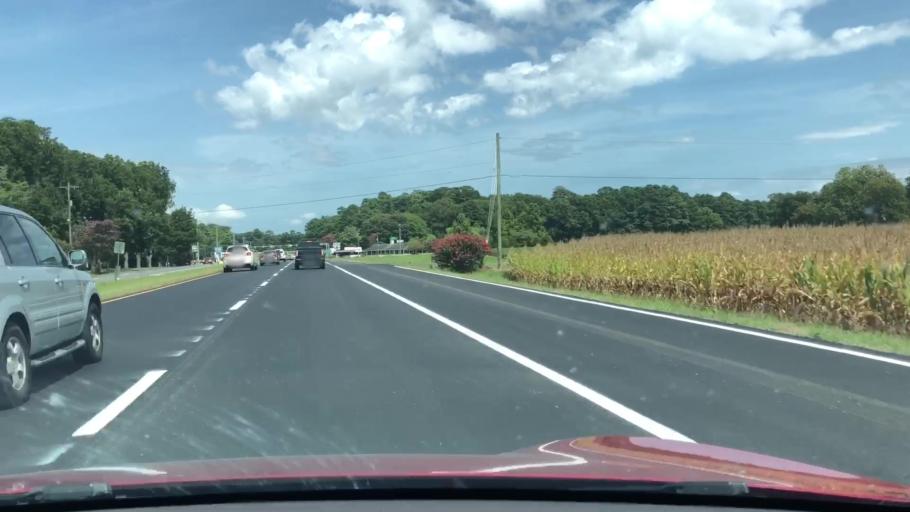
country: US
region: Virginia
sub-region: Accomack County
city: Accomac
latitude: 37.7550
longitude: -75.6244
